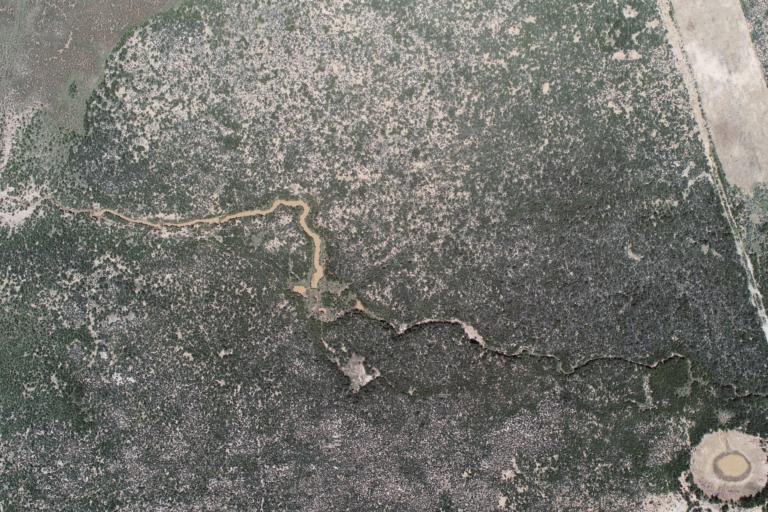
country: BO
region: La Paz
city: Patacamaya
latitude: -17.2927
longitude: -68.4895
